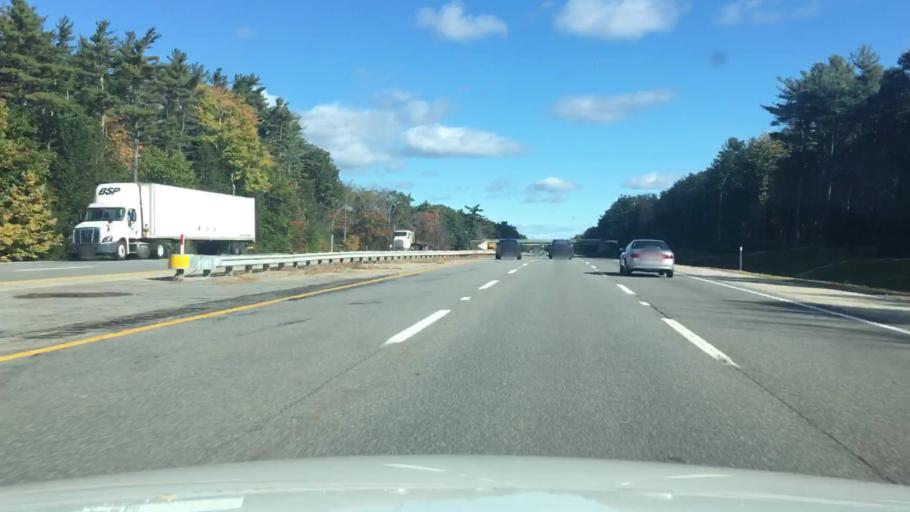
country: US
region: Maine
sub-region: York County
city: Ogunquit
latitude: 43.2450
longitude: -70.6272
